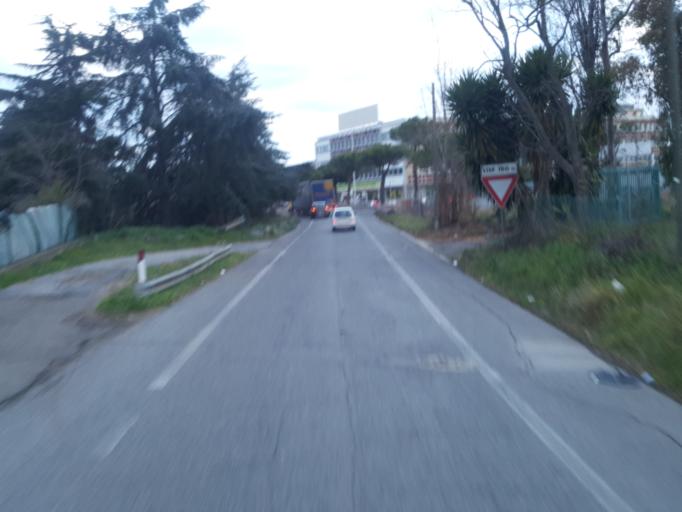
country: IT
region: Latium
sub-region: Citta metropolitana di Roma Capitale
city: Area Produttiva
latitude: 41.6762
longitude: 12.5006
